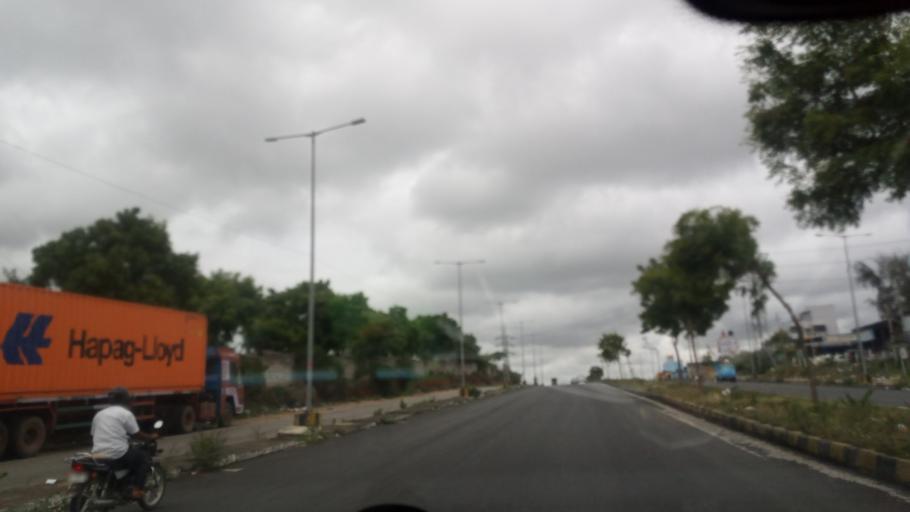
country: IN
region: Karnataka
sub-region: Mysore
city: Mysore
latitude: 12.3544
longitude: 76.6210
